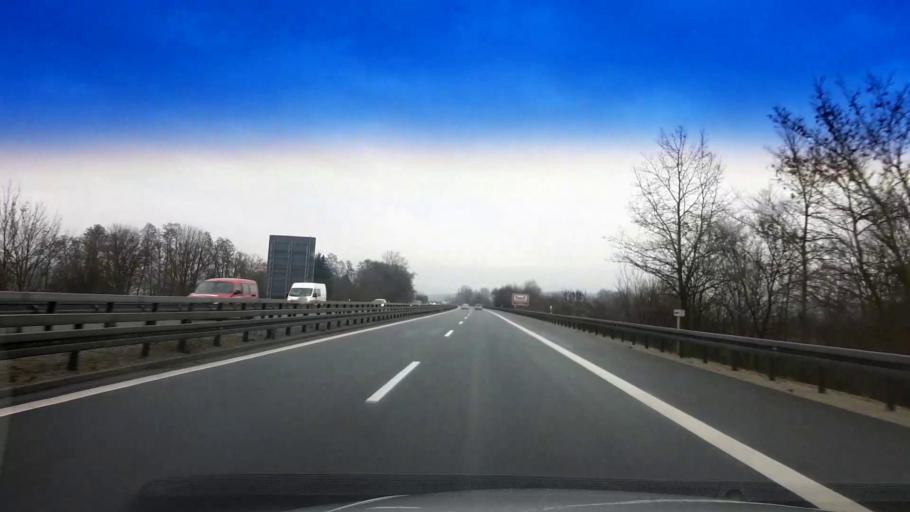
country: DE
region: Bavaria
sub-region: Upper Franconia
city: Gundelsheim
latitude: 49.9337
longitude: 10.9356
